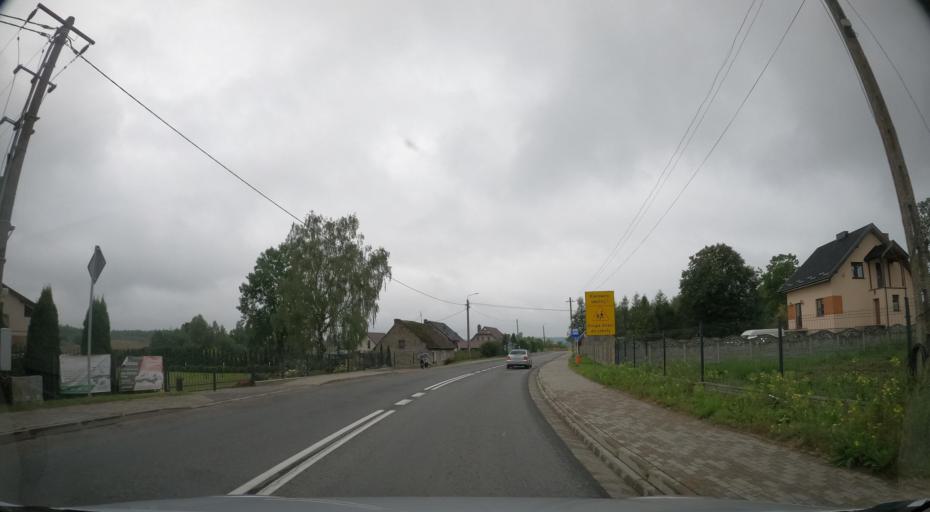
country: PL
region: Pomeranian Voivodeship
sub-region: Powiat wejherowski
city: Linia
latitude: 54.4797
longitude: 17.8562
